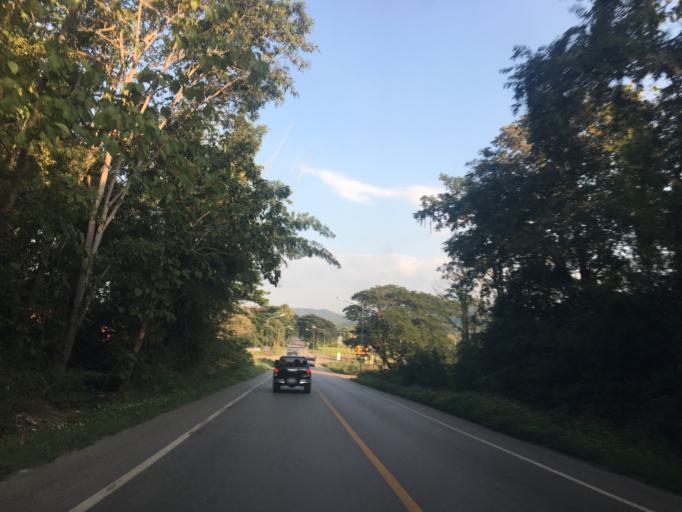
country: TH
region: Lampang
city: Ngao
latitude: 18.6108
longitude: 100.0344
